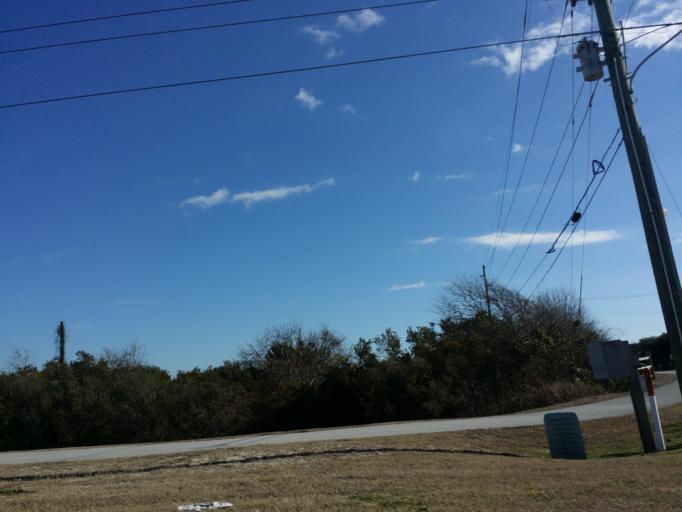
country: US
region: North Carolina
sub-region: Onslow County
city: Sneads Ferry
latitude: 34.4925
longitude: -77.4262
